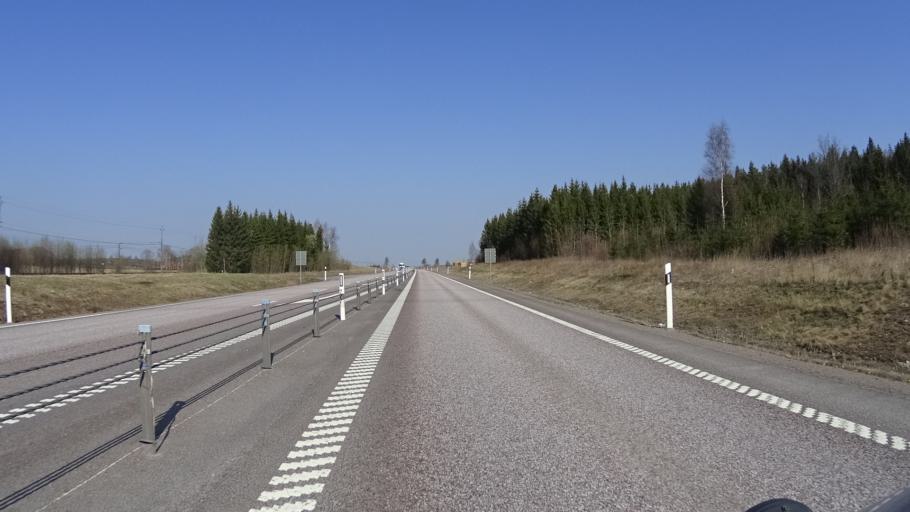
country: SE
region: OEstergoetland
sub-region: Motala Kommun
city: Stenstorp
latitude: 58.4275
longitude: 15.0665
